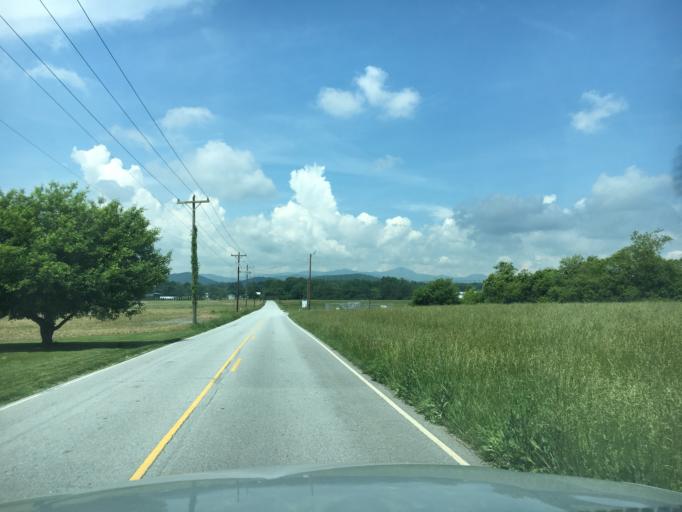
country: US
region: North Carolina
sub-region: Henderson County
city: Mills River
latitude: 35.3774
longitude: -82.5512
